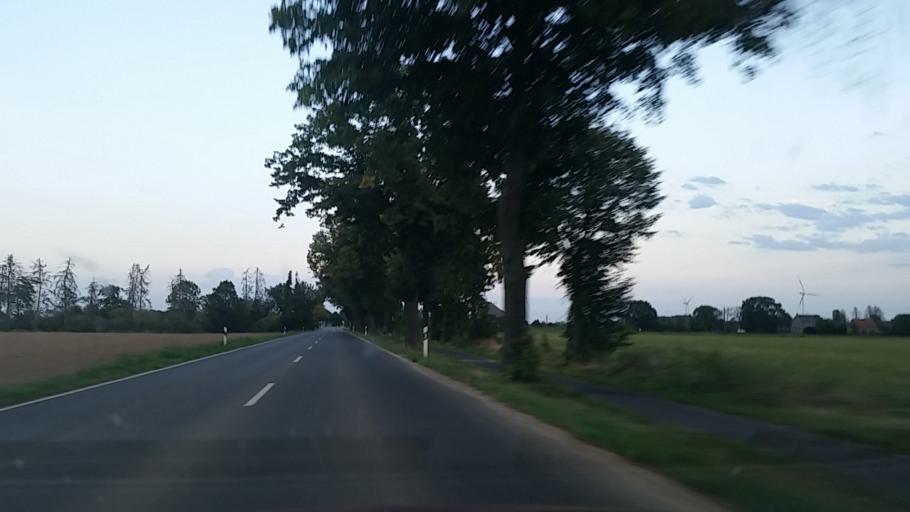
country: DE
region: North Rhine-Westphalia
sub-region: Regierungsbezirk Dusseldorf
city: Willich
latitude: 51.2665
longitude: 6.5647
